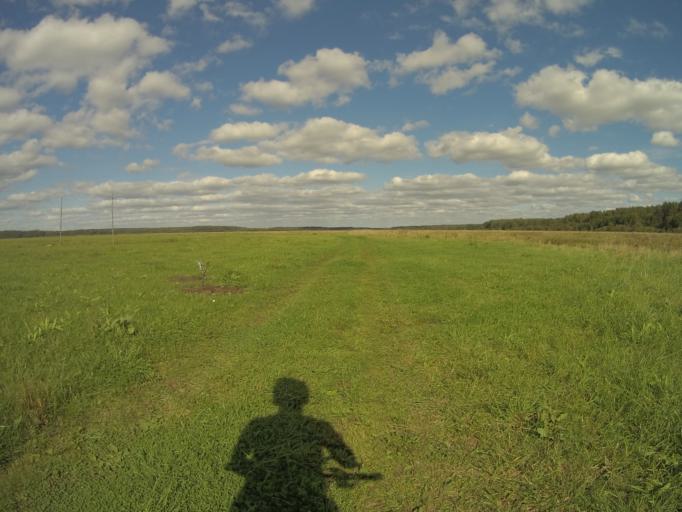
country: RU
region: Vladimir
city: Orgtrud
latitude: 56.3031
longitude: 40.6885
